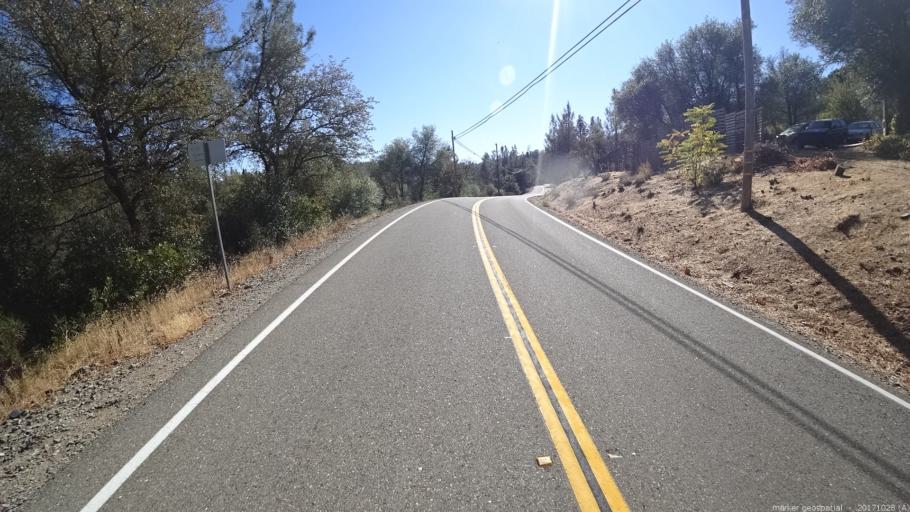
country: US
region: California
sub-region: Shasta County
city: Shasta
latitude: 40.6141
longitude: -122.4915
